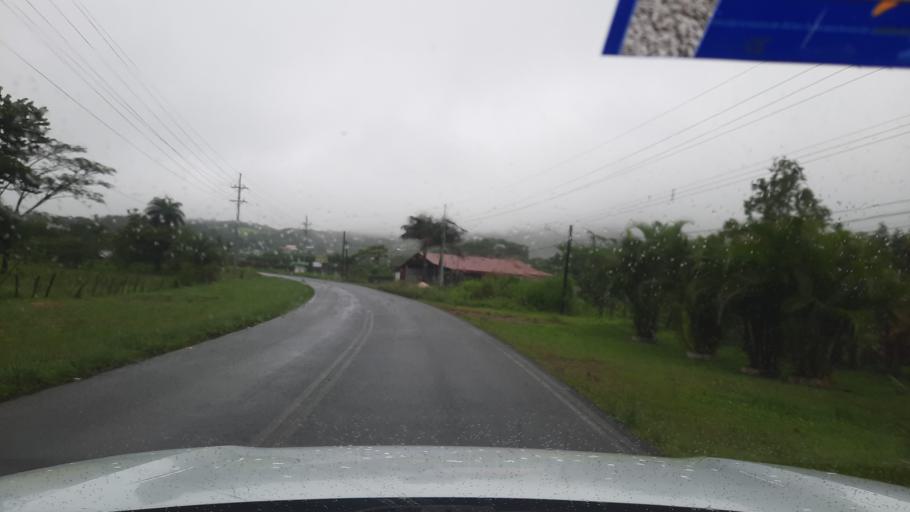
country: CR
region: Alajuela
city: Bijagua
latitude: 10.7230
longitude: -85.0676
